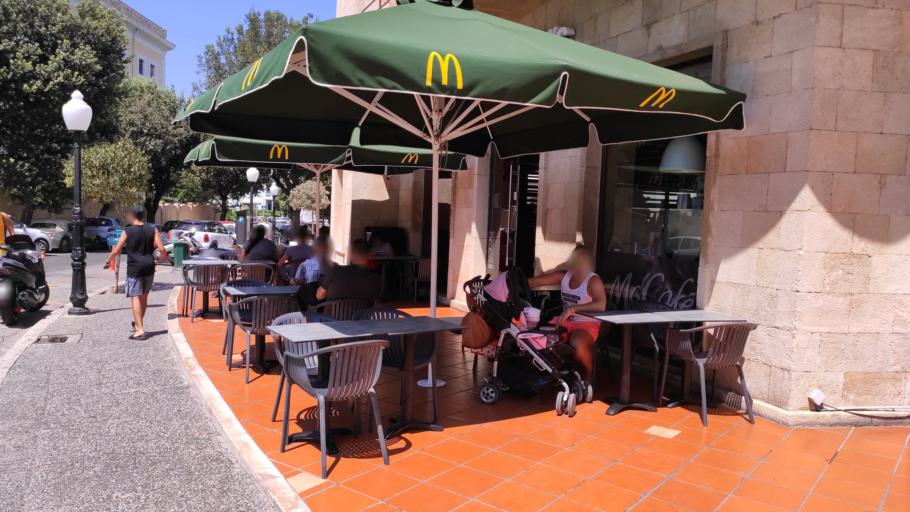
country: GR
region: South Aegean
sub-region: Nomos Dodekanisou
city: Rodos
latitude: 36.4492
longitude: 28.2217
